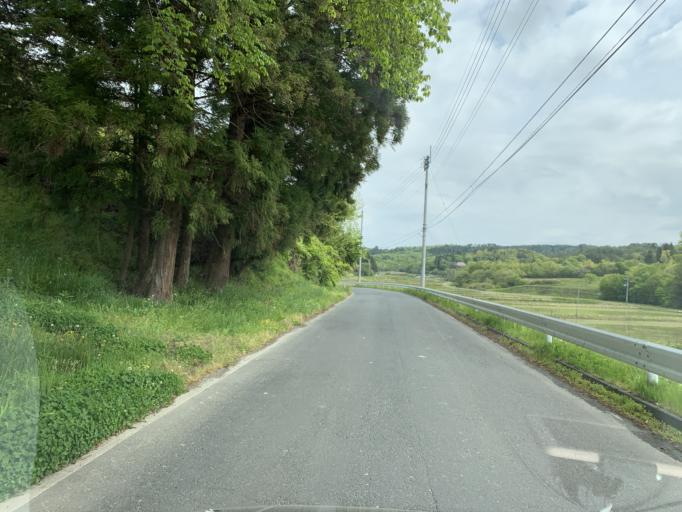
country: JP
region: Iwate
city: Ichinoseki
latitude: 38.8414
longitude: 141.1926
